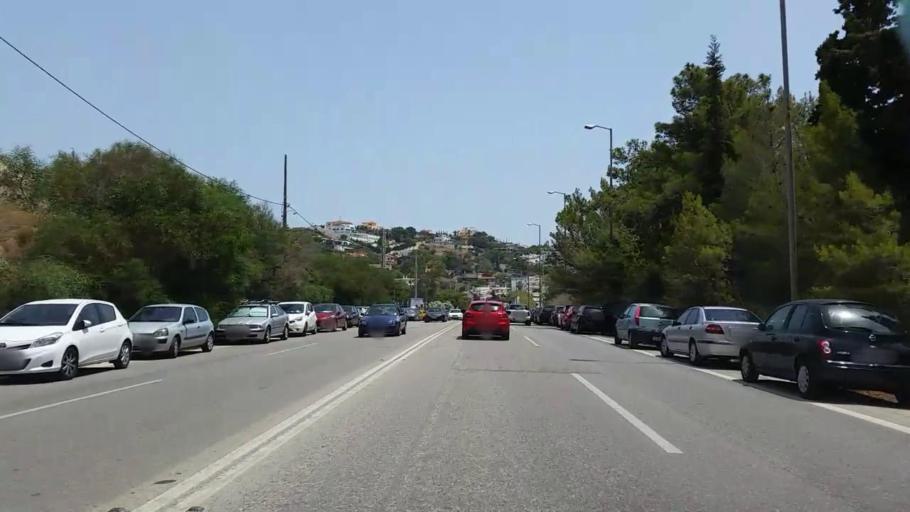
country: GR
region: Attica
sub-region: Nomarchia Anatolikis Attikis
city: Saronida
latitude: 37.7297
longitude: 23.9060
